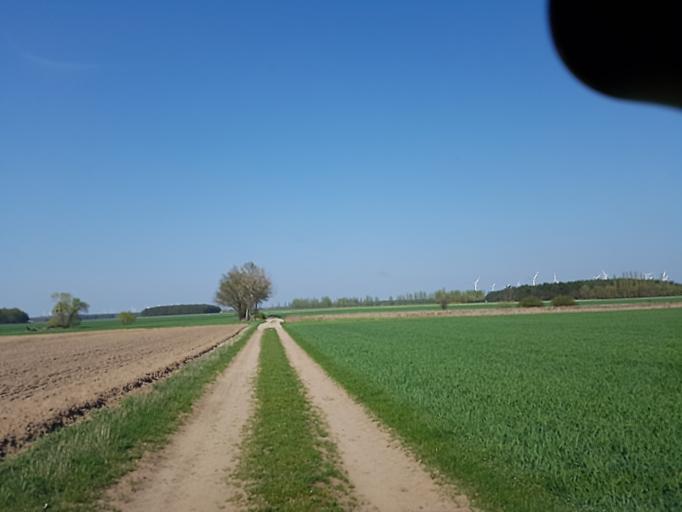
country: DE
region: Brandenburg
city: Falkenberg
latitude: 51.5075
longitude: 13.2827
